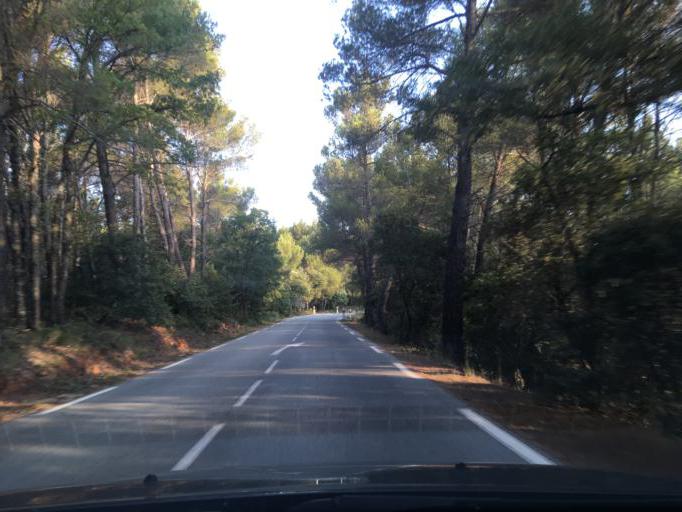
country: FR
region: Provence-Alpes-Cote d'Azur
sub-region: Departement du Var
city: Aups
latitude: 43.6415
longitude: 6.2220
